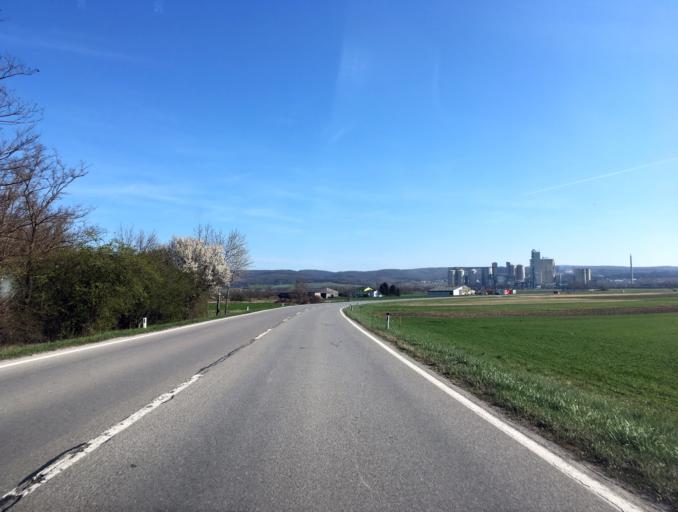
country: AT
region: Lower Austria
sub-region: Politischer Bezirk Bruck an der Leitha
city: Gotzendorf an der Leitha
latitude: 48.0000
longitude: 16.5978
